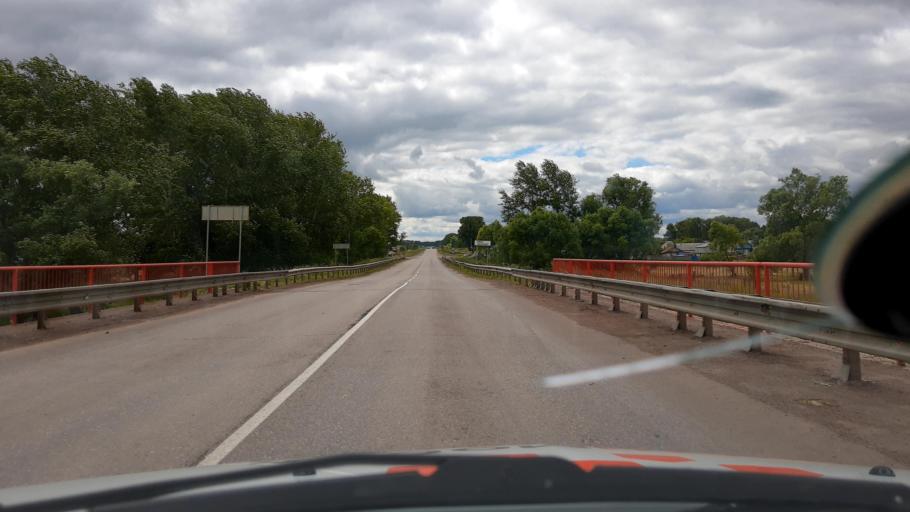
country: RU
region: Bashkortostan
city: Buzdyak
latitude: 54.6903
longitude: 54.5569
